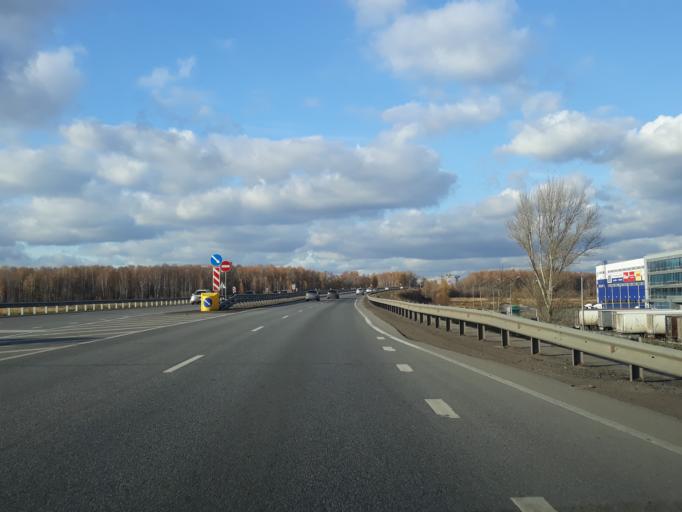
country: RU
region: Nizjnij Novgorod
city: Afonino
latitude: 56.2122
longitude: 44.0814
